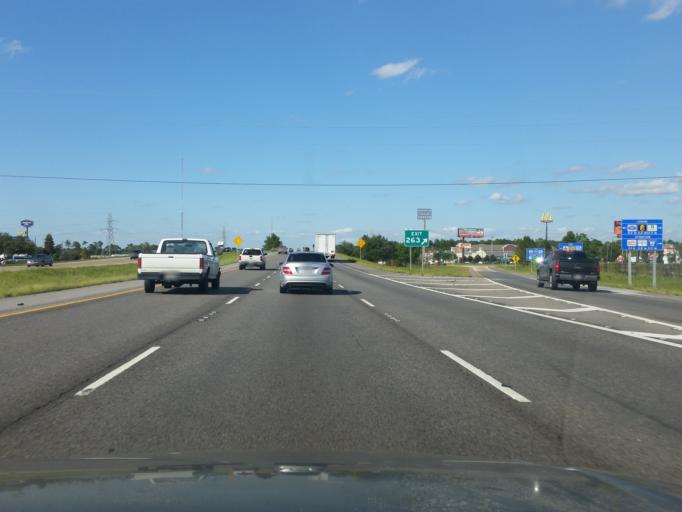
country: US
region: Louisiana
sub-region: Saint Tammany Parish
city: Slidell
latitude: 30.2444
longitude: -89.7645
